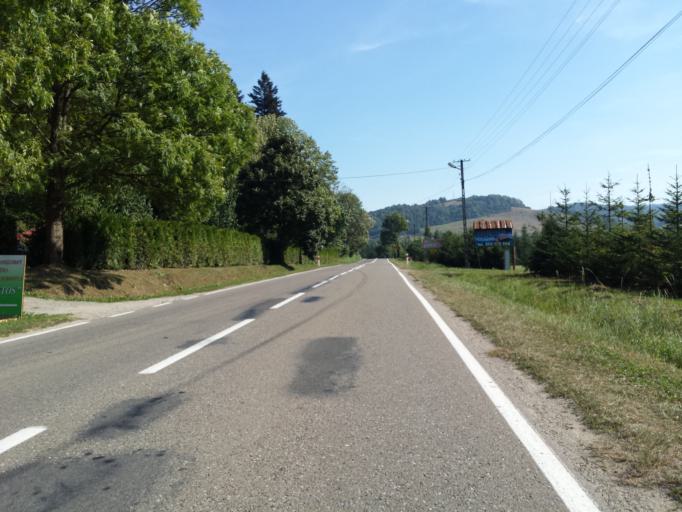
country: PL
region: Subcarpathian Voivodeship
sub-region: Powiat leski
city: Baligrod
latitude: 49.3255
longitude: 22.2816
